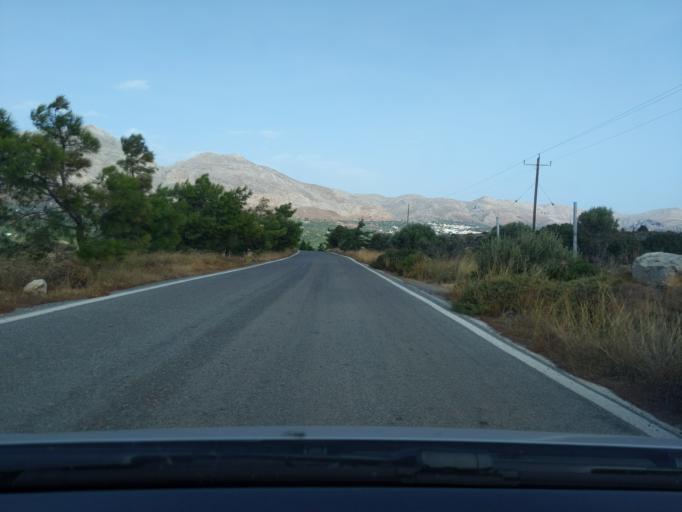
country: GR
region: Crete
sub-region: Nomos Lasithiou
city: Palekastro
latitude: 35.0923
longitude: 26.2363
